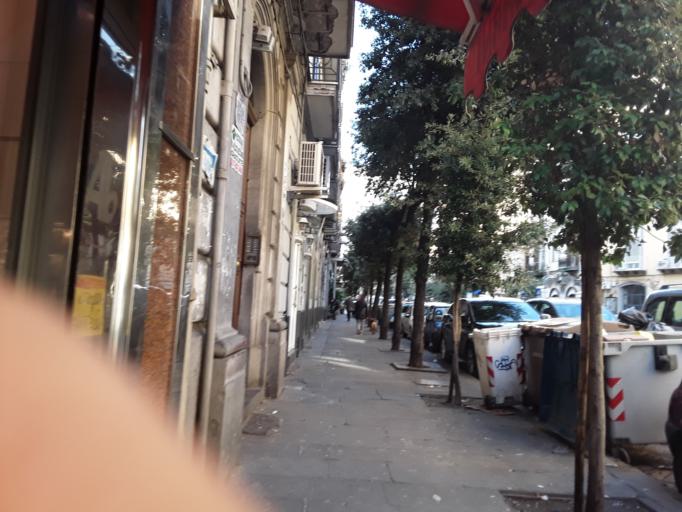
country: IT
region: Campania
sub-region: Provincia di Napoli
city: Napoli
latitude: 40.8579
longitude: 14.2671
